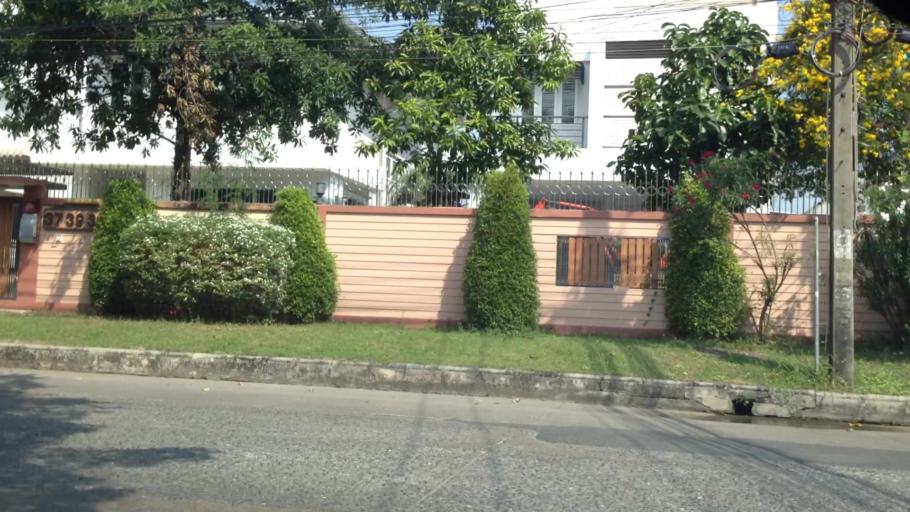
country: TH
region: Bangkok
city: Bang Na
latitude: 13.6859
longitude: 100.6558
